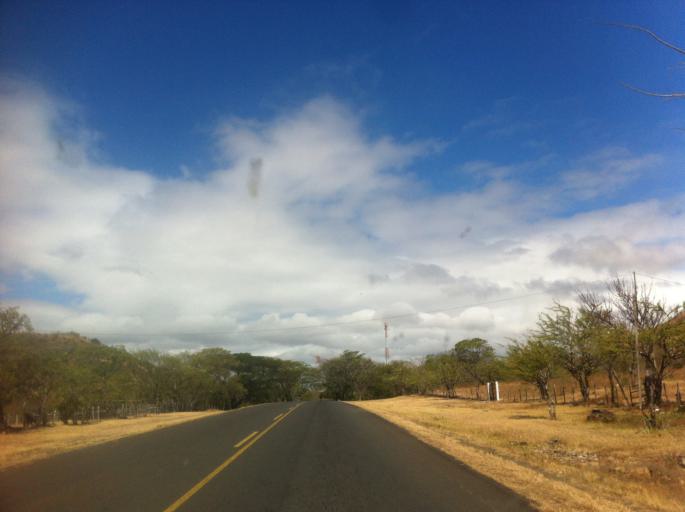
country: NI
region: Chontales
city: Acoyapa
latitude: 12.0163
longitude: -85.2481
